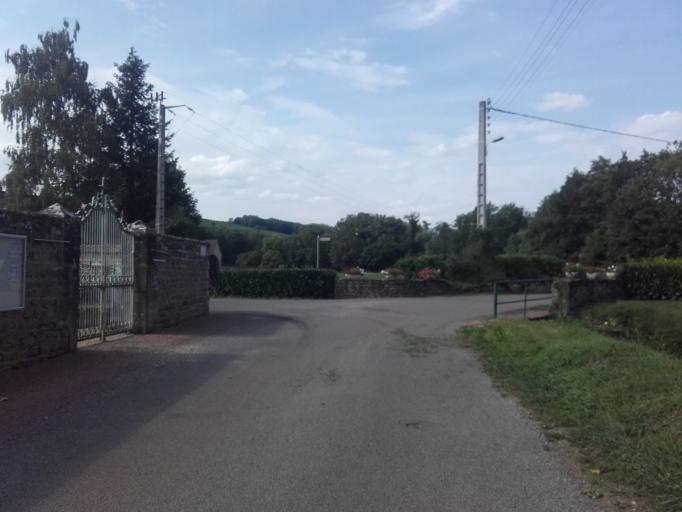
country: FR
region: Bourgogne
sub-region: Departement de la Cote-d'Or
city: Nolay
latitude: 46.9167
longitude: 4.6342
